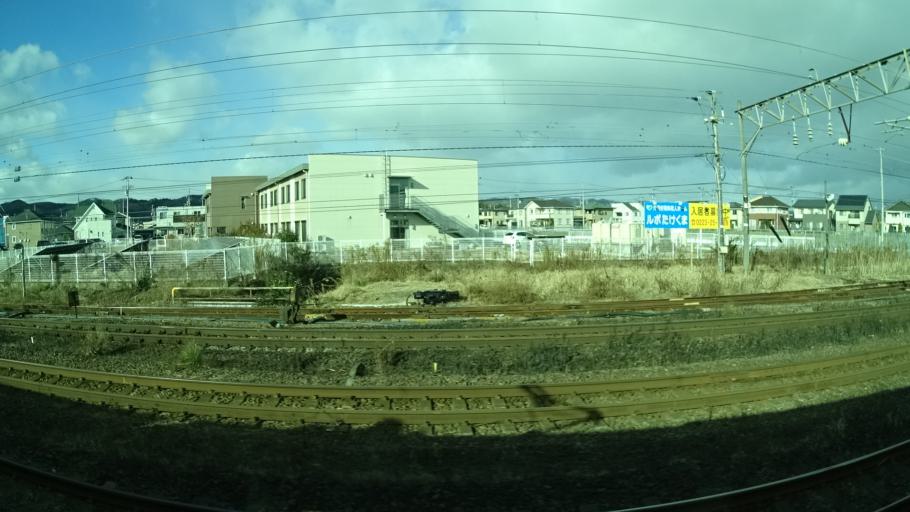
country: JP
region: Miyagi
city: Iwanuma
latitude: 38.1094
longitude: 140.8617
